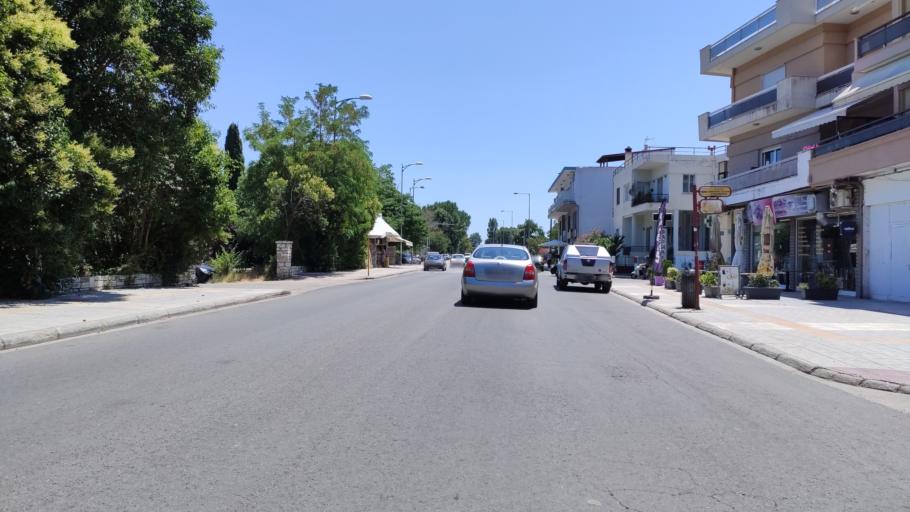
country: GR
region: East Macedonia and Thrace
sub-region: Nomos Rodopis
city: Komotini
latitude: 41.1129
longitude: 25.4110
